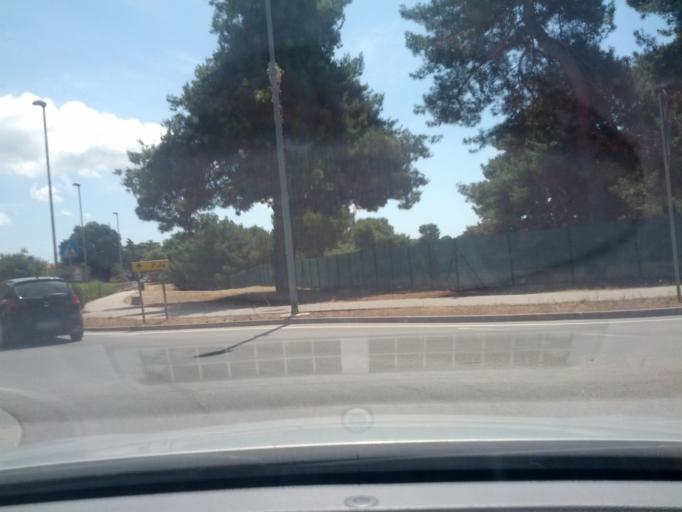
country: HR
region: Istarska
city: Fazana
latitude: 44.9157
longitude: 13.8150
